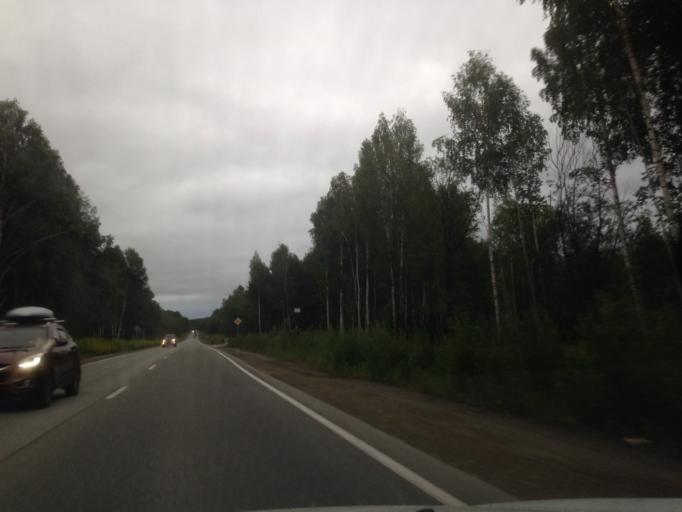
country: RU
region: Sverdlovsk
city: Istok
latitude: 56.8423
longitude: 60.7405
